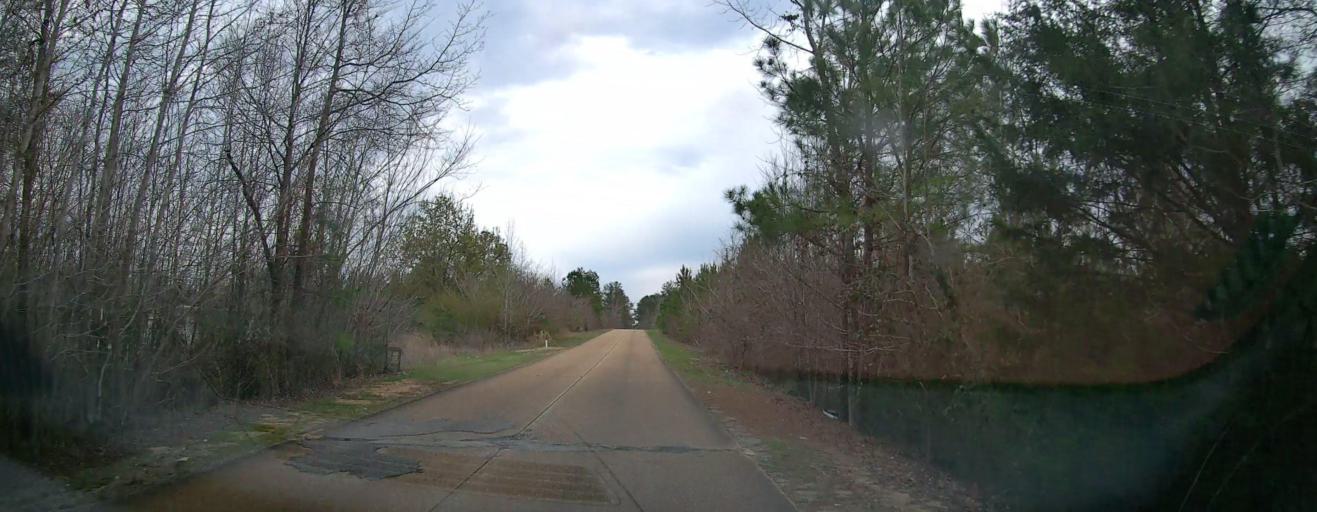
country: US
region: Mississippi
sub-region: Itawamba County
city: Fulton
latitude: 34.2117
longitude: -88.1990
